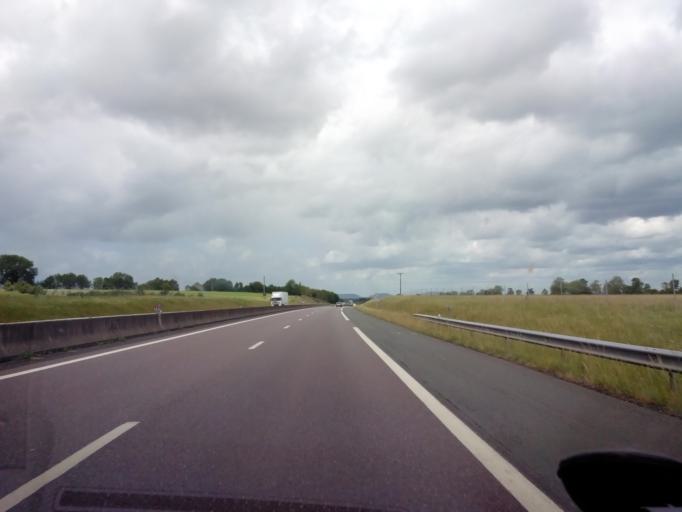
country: FR
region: Lorraine
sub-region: Departement de Meurthe-et-Moselle
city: Colombey-les-Belles
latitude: 48.5527
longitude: 5.8928
